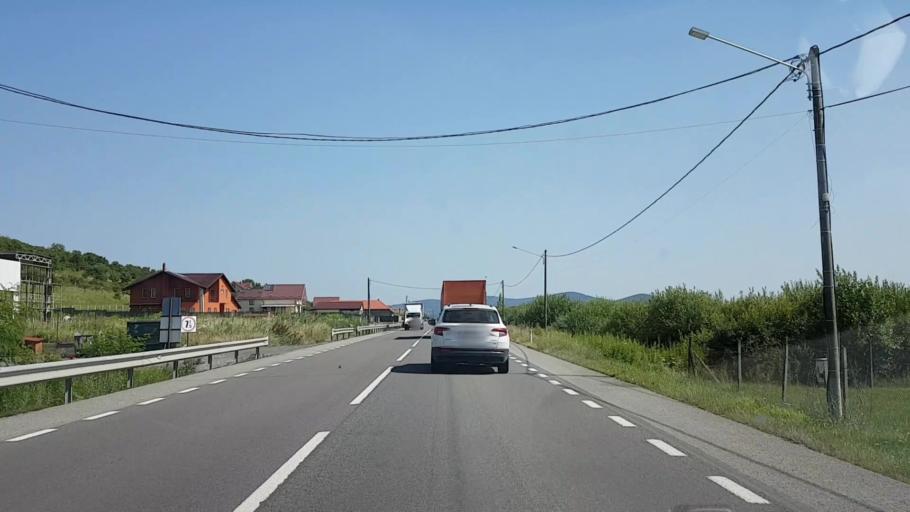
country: RO
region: Bistrita-Nasaud
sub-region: Comuna Sieu-Odorhei
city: Sieu-Odorhei
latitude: 47.1349
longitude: 24.3085
